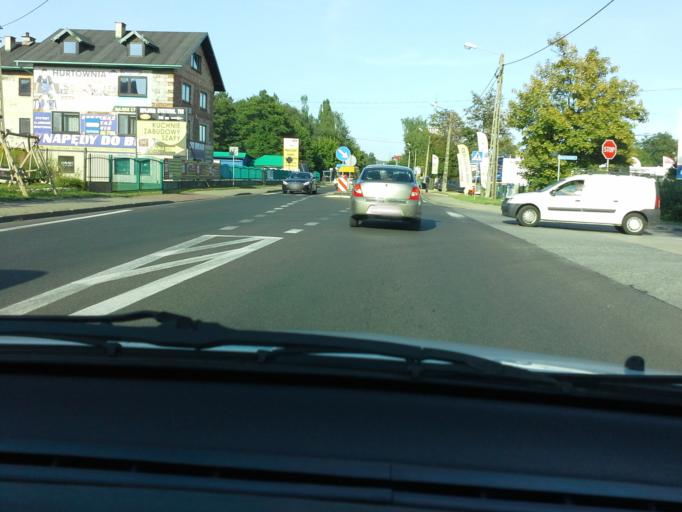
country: PL
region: Lesser Poland Voivodeship
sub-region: Powiat chrzanowski
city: Trzebinia
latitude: 50.1514
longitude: 19.4408
